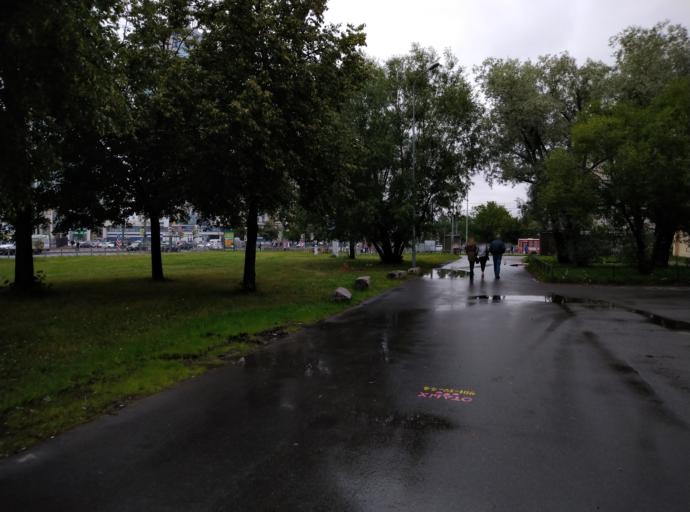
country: RU
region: St.-Petersburg
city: Kupchino
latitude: 59.8518
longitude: 30.3537
